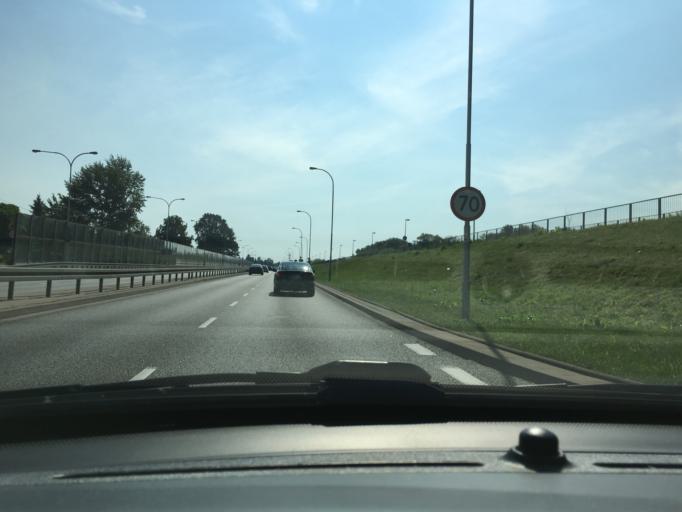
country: PL
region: Masovian Voivodeship
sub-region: Warszawa
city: Praga Poludnie
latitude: 52.2111
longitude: 21.1057
